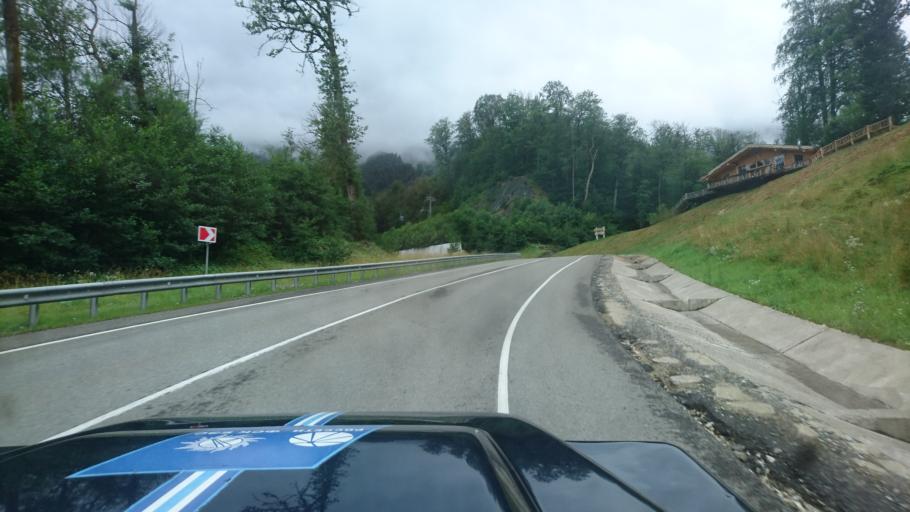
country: RU
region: Krasnodarskiy
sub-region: Sochi City
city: Krasnaya Polyana
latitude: 43.6671
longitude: 40.3003
